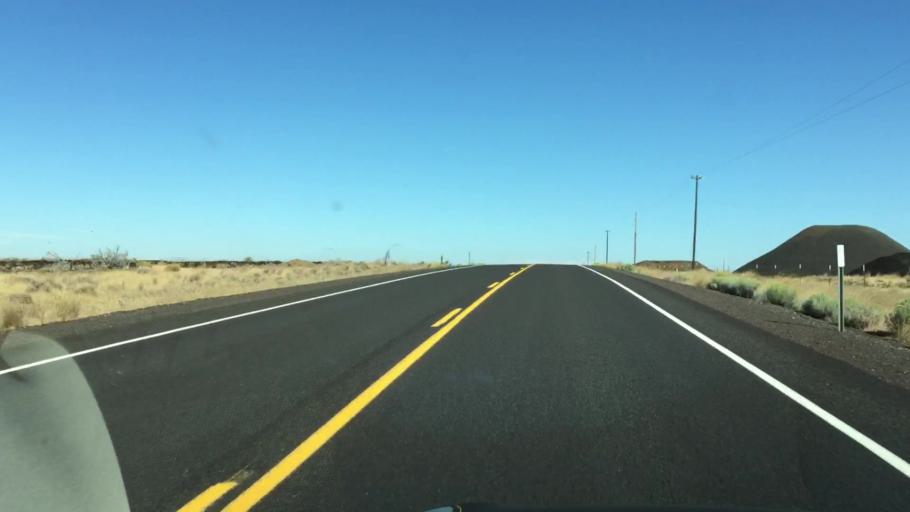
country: US
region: Oregon
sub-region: Jefferson County
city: Warm Springs
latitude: 44.9798
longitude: -120.9898
